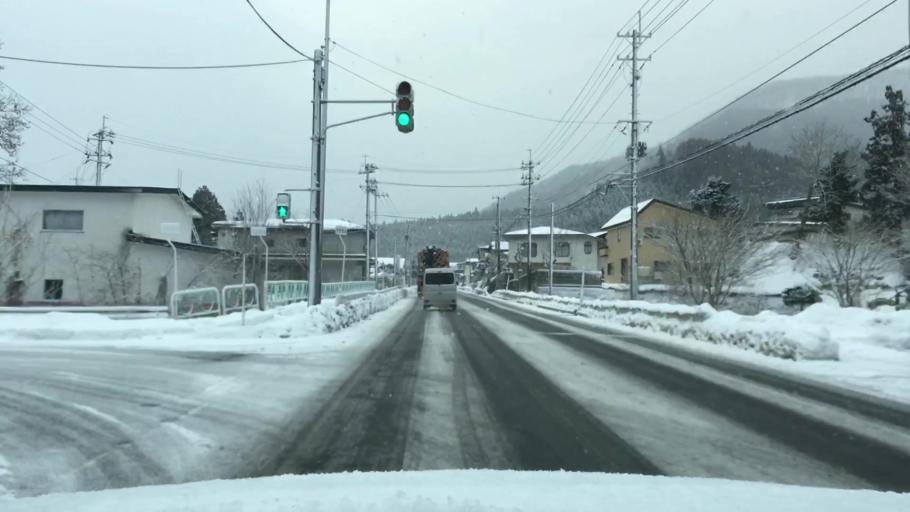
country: JP
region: Aomori
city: Kuroishi
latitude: 40.5035
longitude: 140.6126
